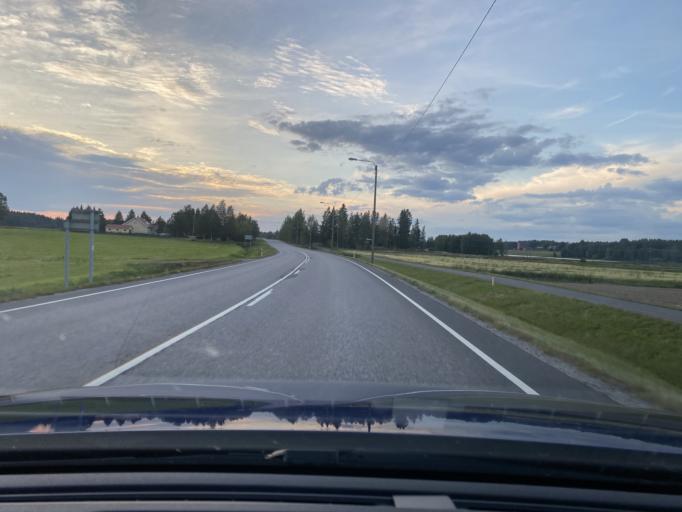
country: FI
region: Satakunta
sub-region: Pohjois-Satakunta
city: Kankaanpaeae
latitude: 61.7451
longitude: 22.5234
